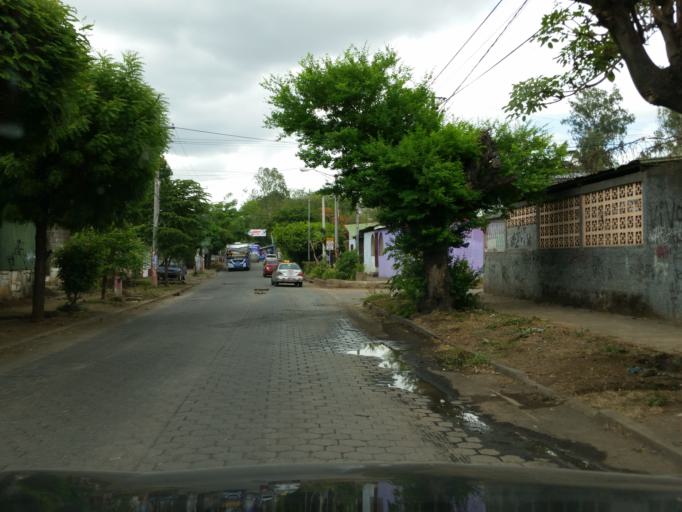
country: NI
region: Managua
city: Managua
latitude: 12.1382
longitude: -86.2254
